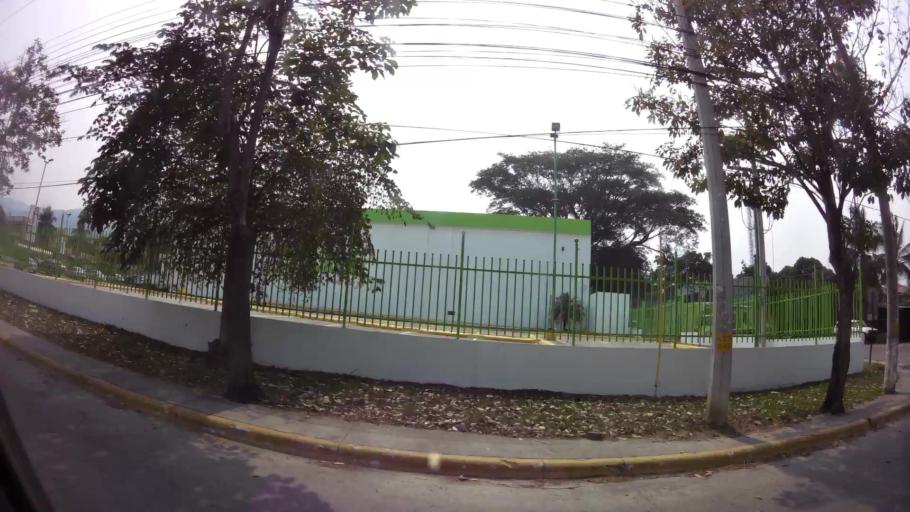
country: HN
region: Cortes
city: San Pedro Sula
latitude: 15.4856
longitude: -88.0332
